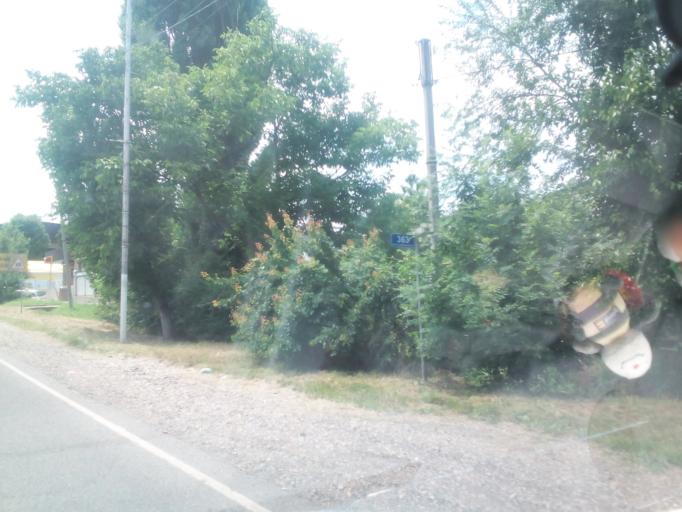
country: RU
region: Stavropol'skiy
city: Inozemtsevo
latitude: 44.1020
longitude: 43.0911
